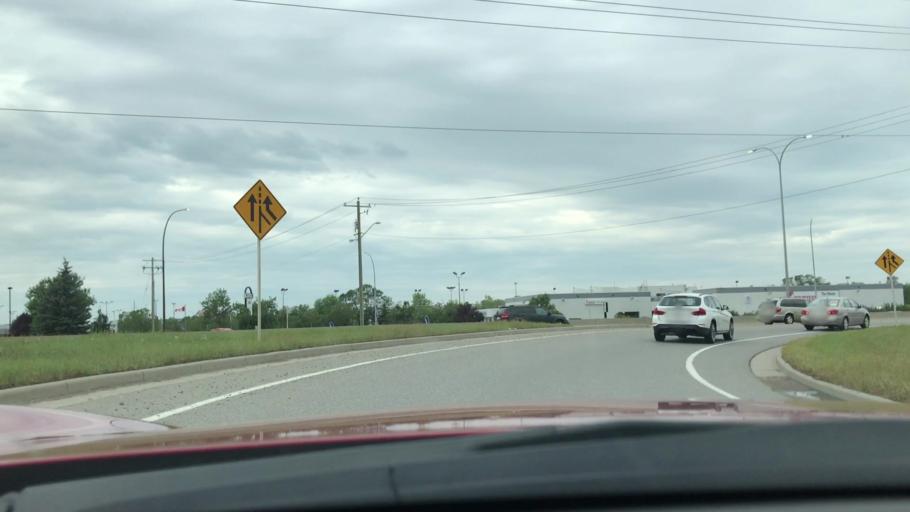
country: CA
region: Alberta
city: Calgary
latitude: 50.9894
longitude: -114.0270
